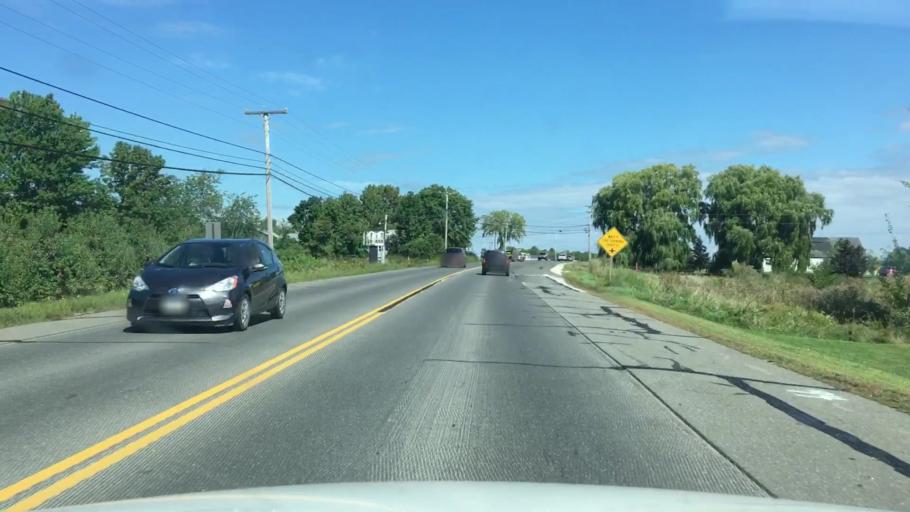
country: US
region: Maine
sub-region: Penobscot County
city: Newport
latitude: 44.8588
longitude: -69.2843
